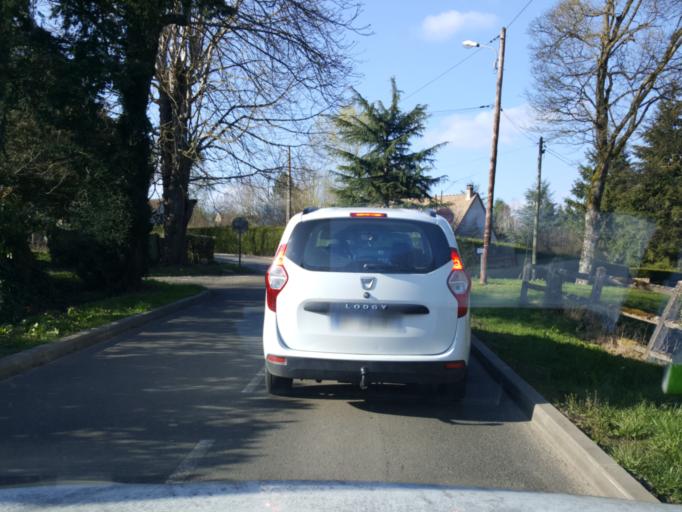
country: FR
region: Ile-de-France
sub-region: Departement des Yvelines
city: Gazeran
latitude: 48.6349
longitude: 1.7655
